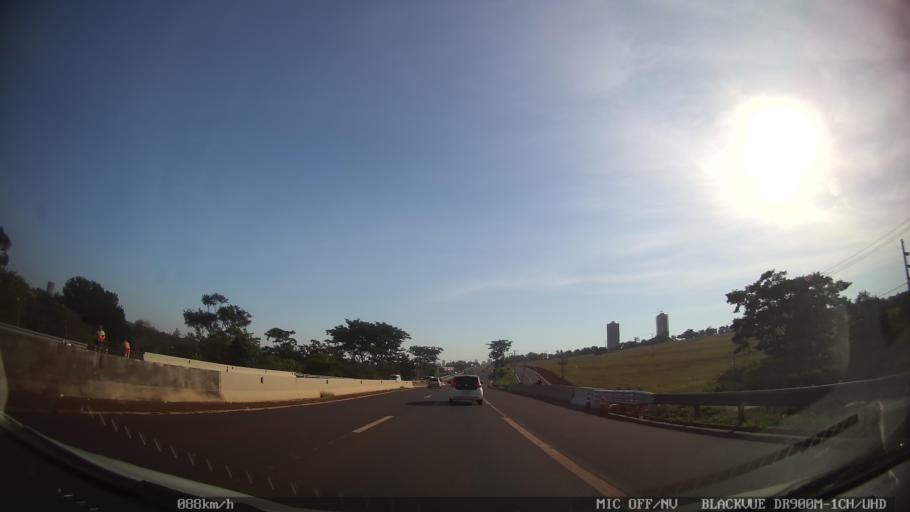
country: BR
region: Sao Paulo
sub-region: Ribeirao Preto
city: Ribeirao Preto
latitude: -21.2492
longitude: -47.8194
